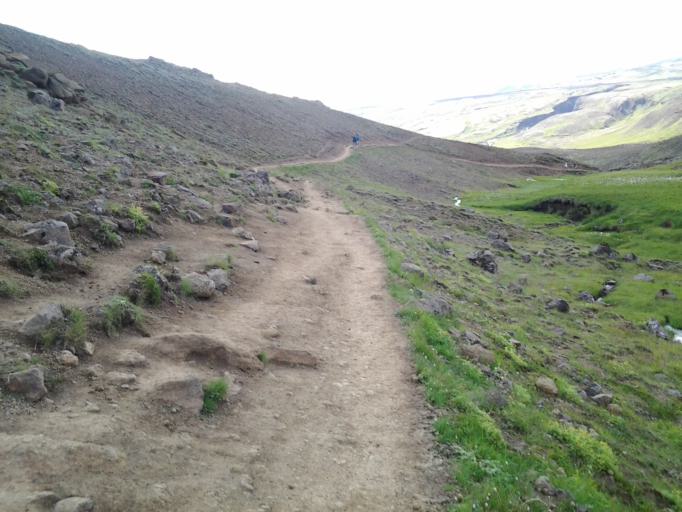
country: IS
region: South
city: Hveragerdi
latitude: 64.0298
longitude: -21.2151
